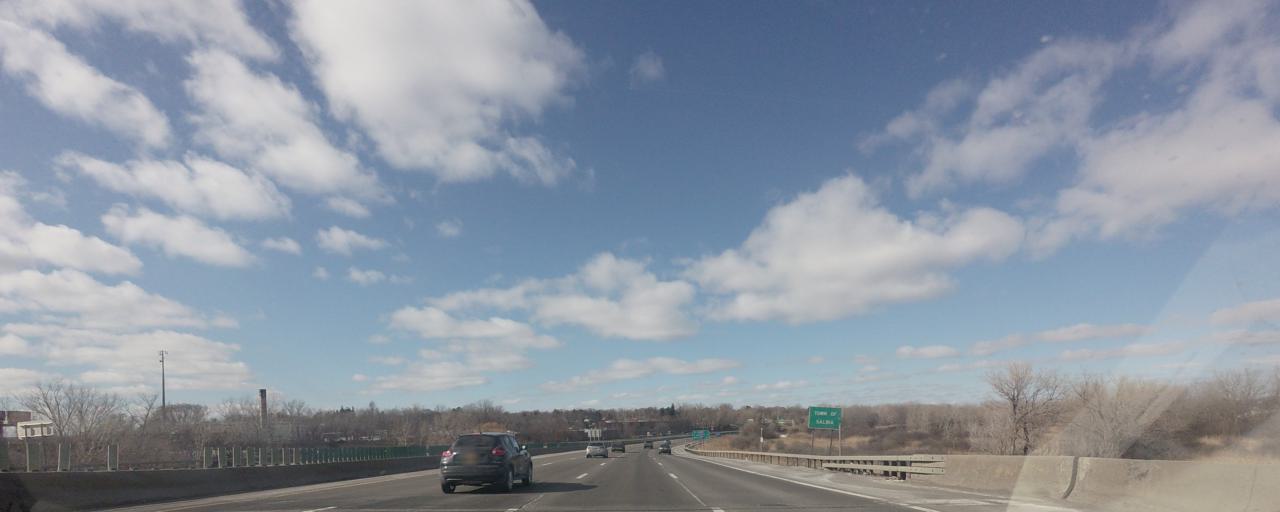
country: US
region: New York
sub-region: Onondaga County
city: Galeville
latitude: 43.0775
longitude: -76.1721
